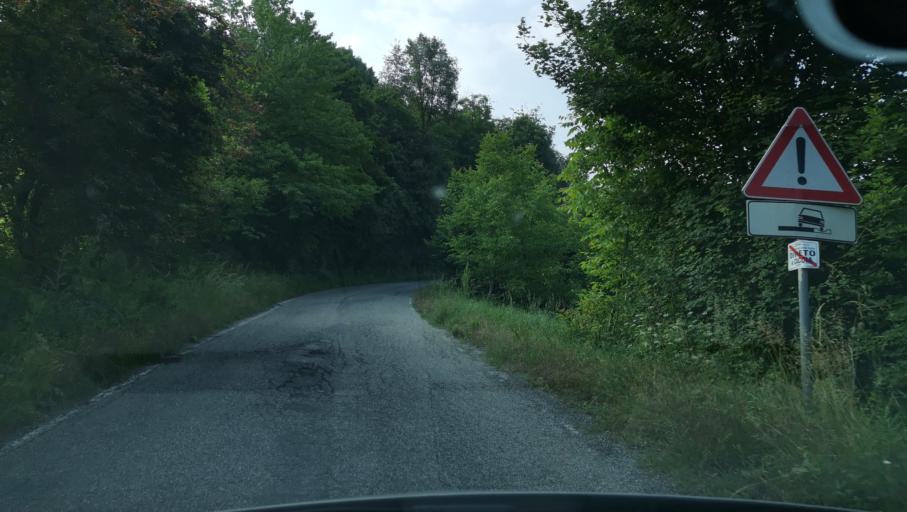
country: IT
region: Piedmont
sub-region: Provincia di Alessandria
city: Odalengo Piccolo
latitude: 45.0743
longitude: 8.1975
